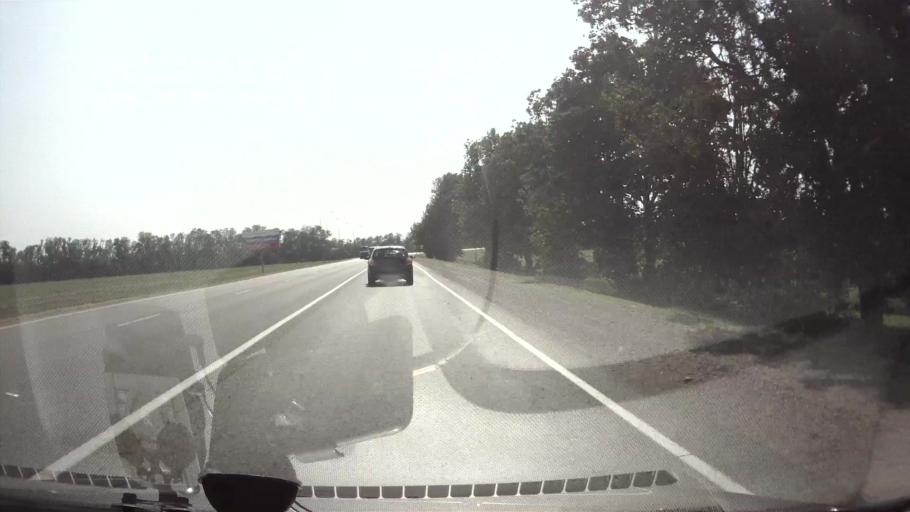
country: RU
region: Krasnodarskiy
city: Vasyurinskaya
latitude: 45.1005
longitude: 39.3867
